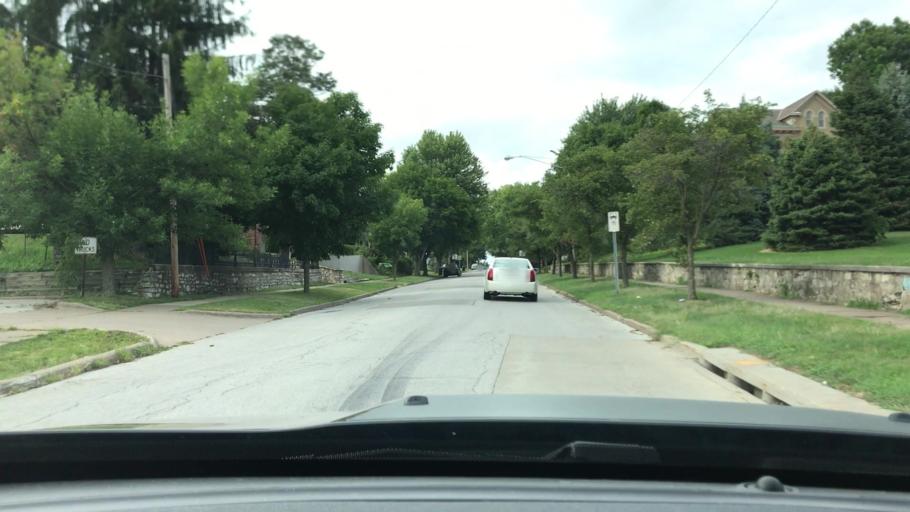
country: US
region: Iowa
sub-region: Scott County
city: Davenport
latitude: 41.5272
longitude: -90.5578
